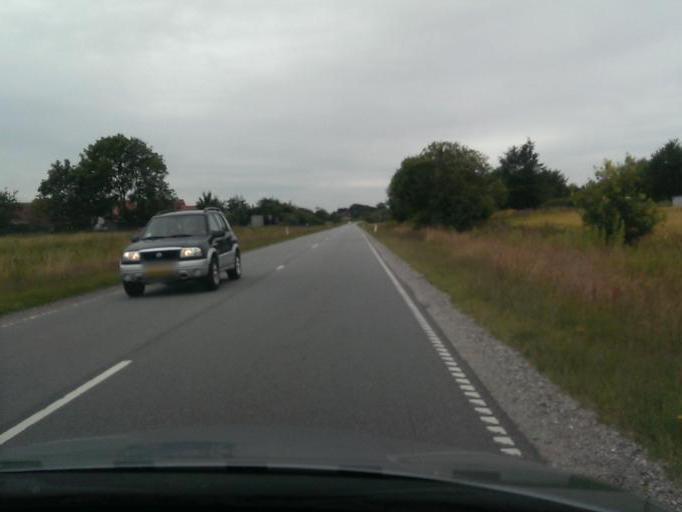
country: DK
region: North Denmark
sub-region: Hjorring Kommune
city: Vra
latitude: 57.3557
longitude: 9.9207
